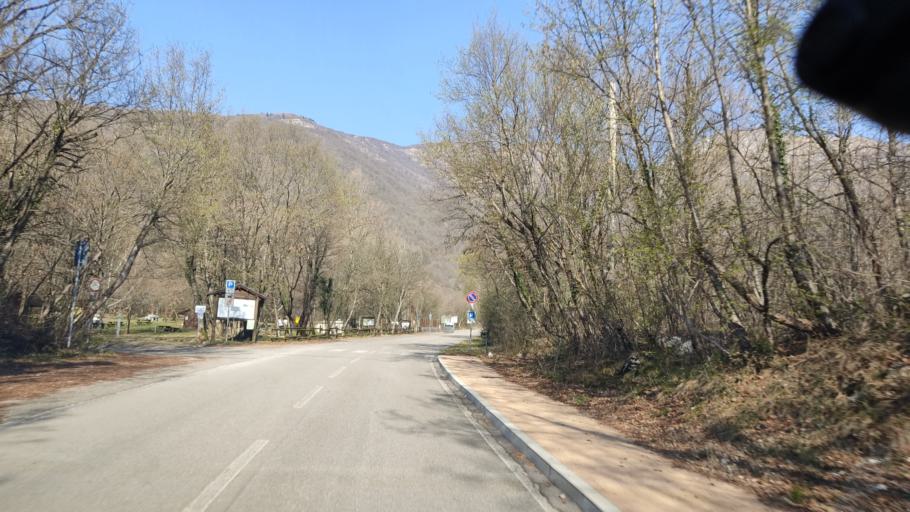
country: IT
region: Friuli Venezia Giulia
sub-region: Provincia di Pordenone
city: Budoia
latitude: 46.0588
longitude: 12.5232
